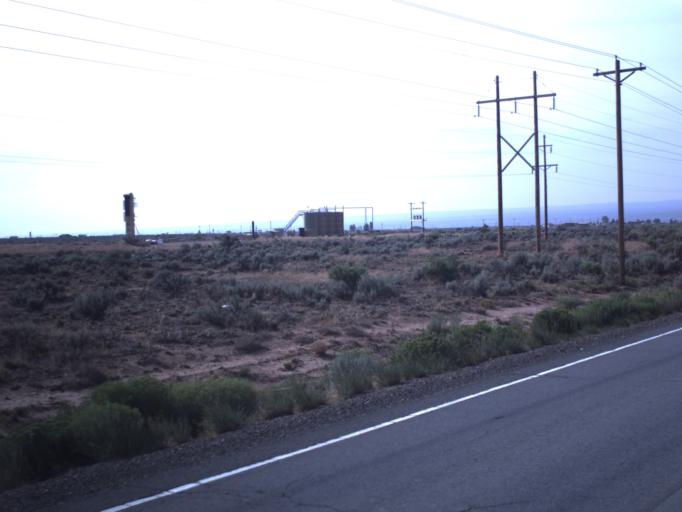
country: US
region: Utah
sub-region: Duchesne County
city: Duchesne
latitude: 40.2417
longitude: -110.3886
